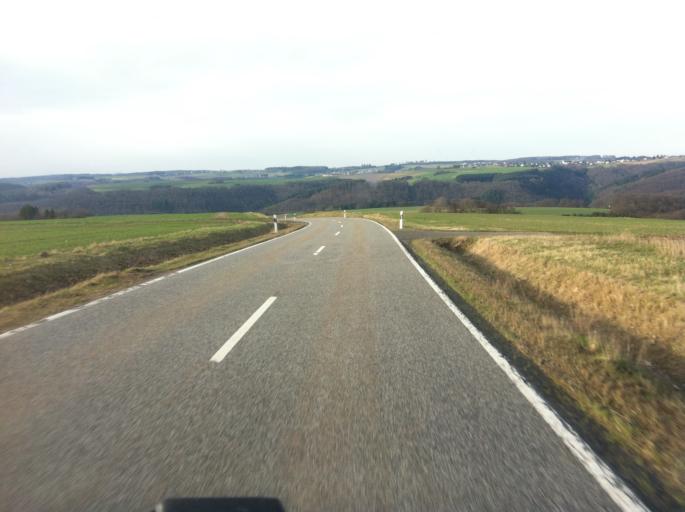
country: DE
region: Rheinland-Pfalz
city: Altlay
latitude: 49.9793
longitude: 7.2827
